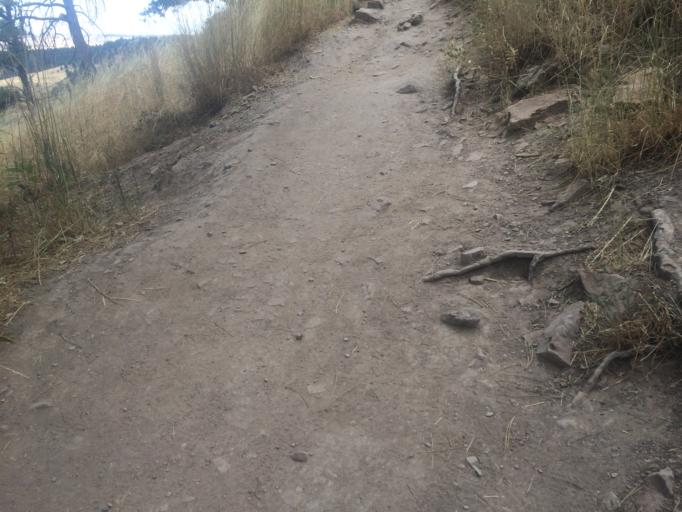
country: US
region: Colorado
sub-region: Boulder County
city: Boulder
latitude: 39.9779
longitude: -105.2805
